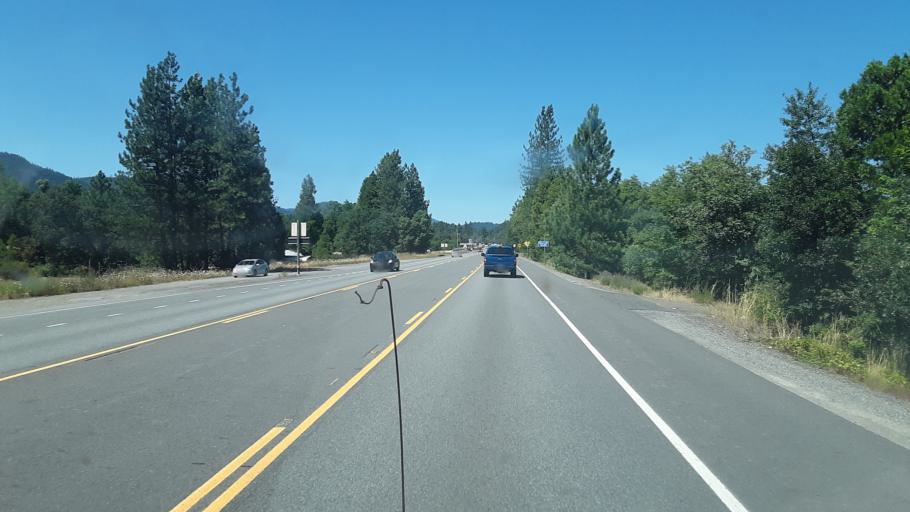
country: US
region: Oregon
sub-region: Josephine County
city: Cave Junction
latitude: 42.2737
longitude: -123.6180
